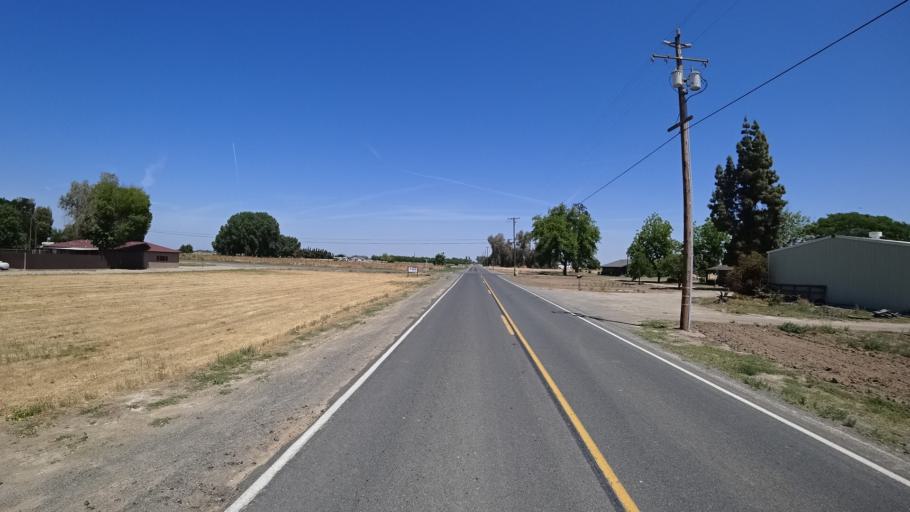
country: US
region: California
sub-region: Kings County
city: Armona
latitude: 36.2541
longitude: -119.7090
